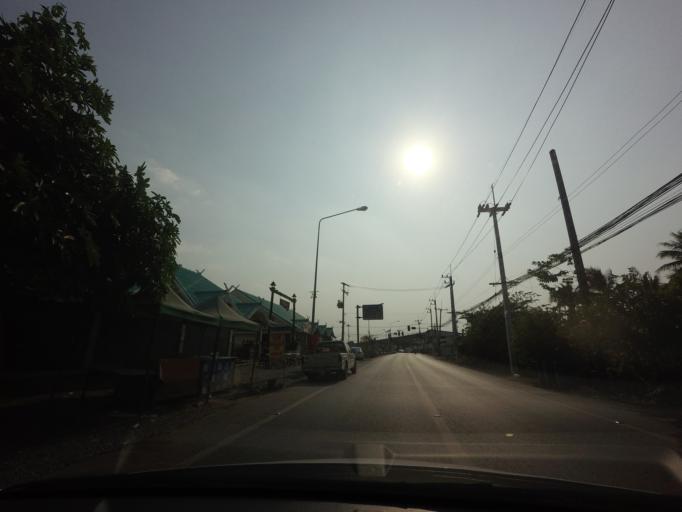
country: TH
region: Nakhon Pathom
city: Sam Phran
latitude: 13.6949
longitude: 100.2342
